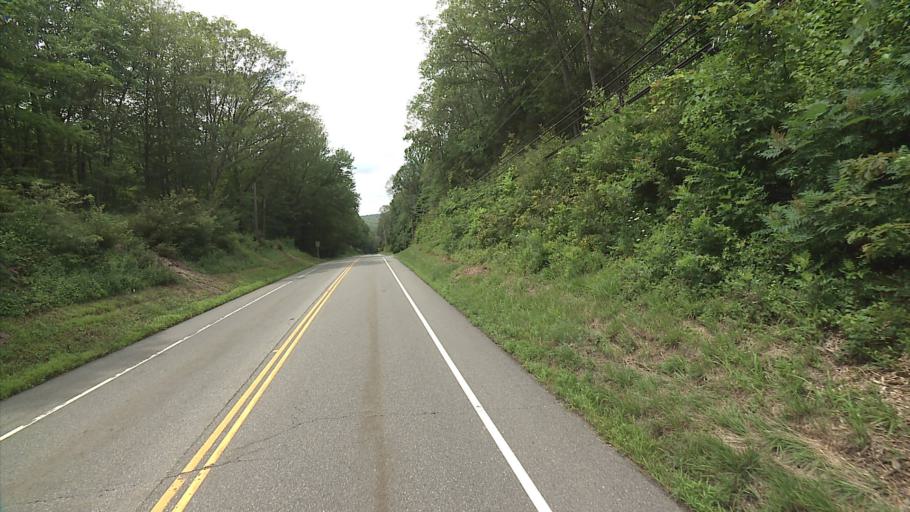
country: US
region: Connecticut
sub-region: New Haven County
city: Madison
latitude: 41.3586
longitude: -72.5707
